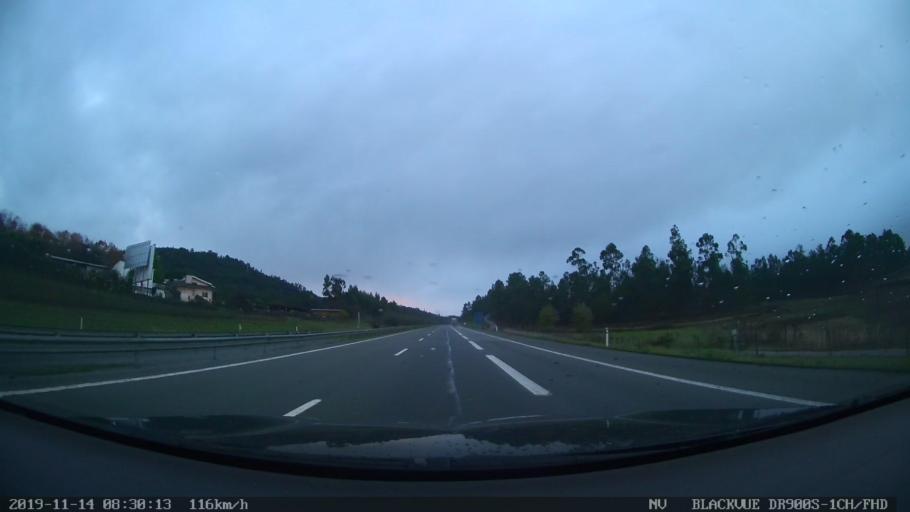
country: PT
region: Braga
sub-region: Barcelos
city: Galegos
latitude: 41.5699
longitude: -8.5490
